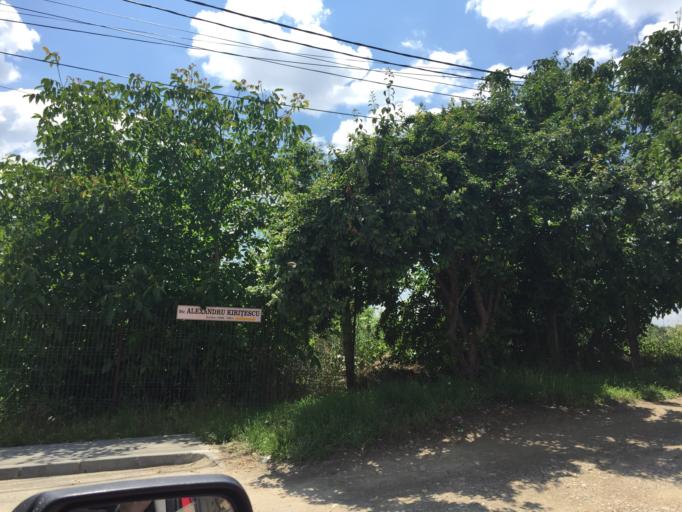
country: RO
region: Cluj
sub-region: Municipiul Cluj-Napoca
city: Cluj-Napoca
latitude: 46.7971
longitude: 23.6026
